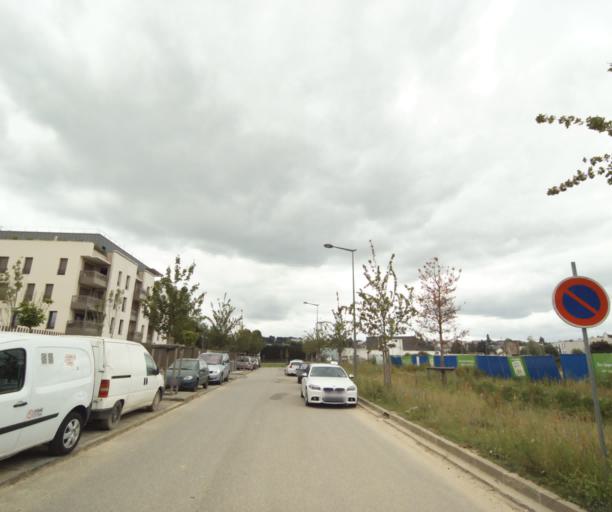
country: FR
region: Ile-de-France
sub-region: Departement des Yvelines
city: Saint-Cyr-l'Ecole
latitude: 48.8067
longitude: 2.0653
